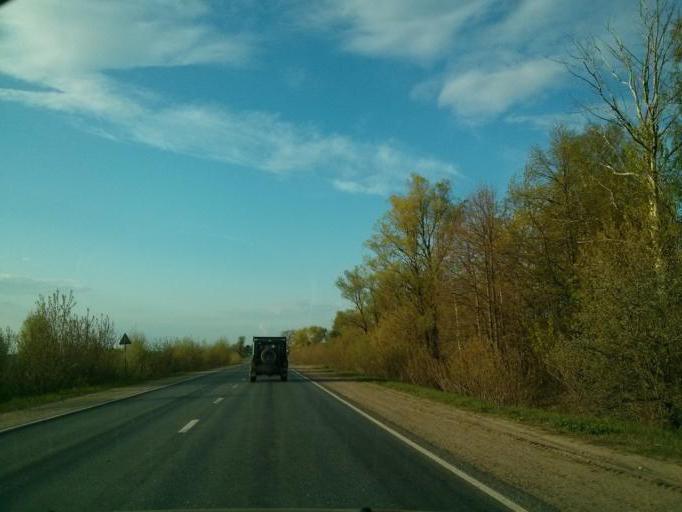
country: RU
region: Nizjnij Novgorod
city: Navashino
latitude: 55.6241
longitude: 42.2308
